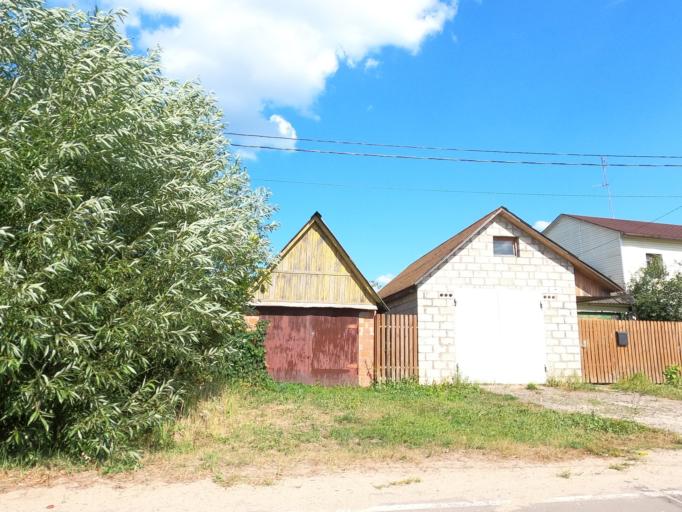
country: RU
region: Moskovskaya
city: Peski
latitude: 55.2266
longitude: 38.7510
